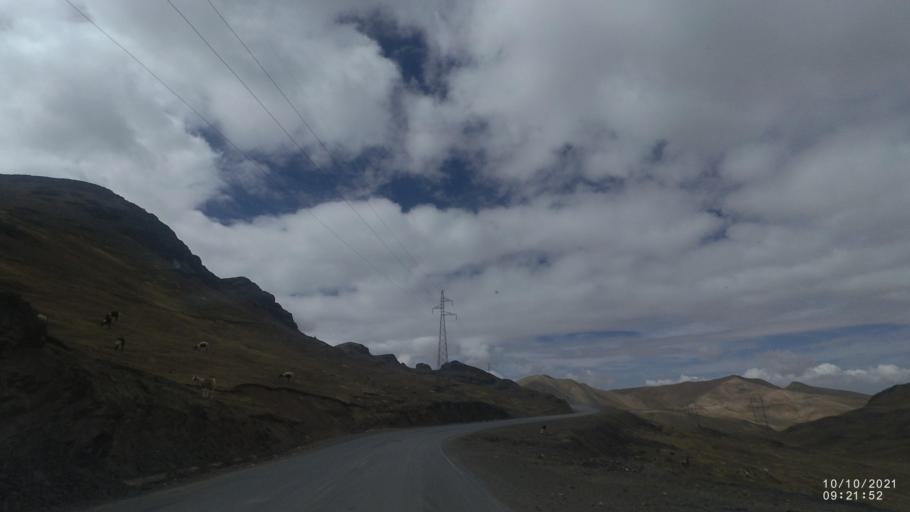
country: BO
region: La Paz
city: Quime
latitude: -17.0719
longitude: -67.2988
